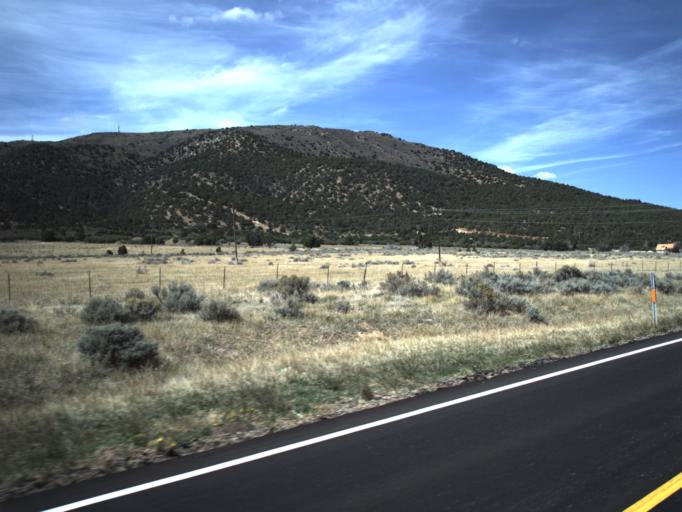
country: US
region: Utah
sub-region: Washington County
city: Enterprise
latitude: 37.4985
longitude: -113.6314
